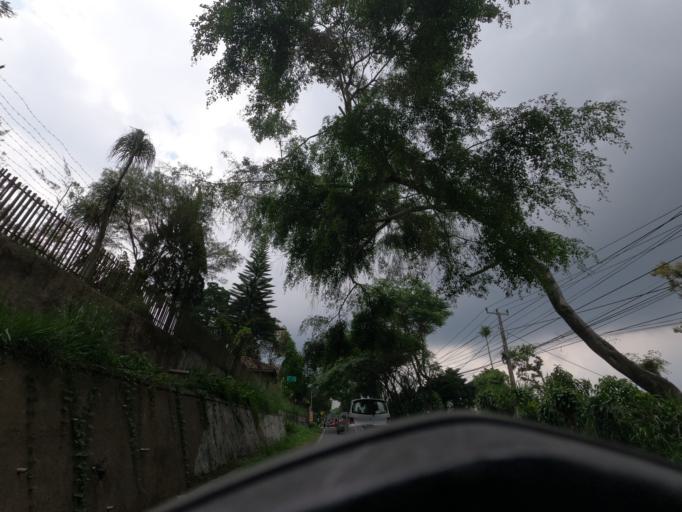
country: ID
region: West Java
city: Sukabumi
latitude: -6.7662
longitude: 107.0557
